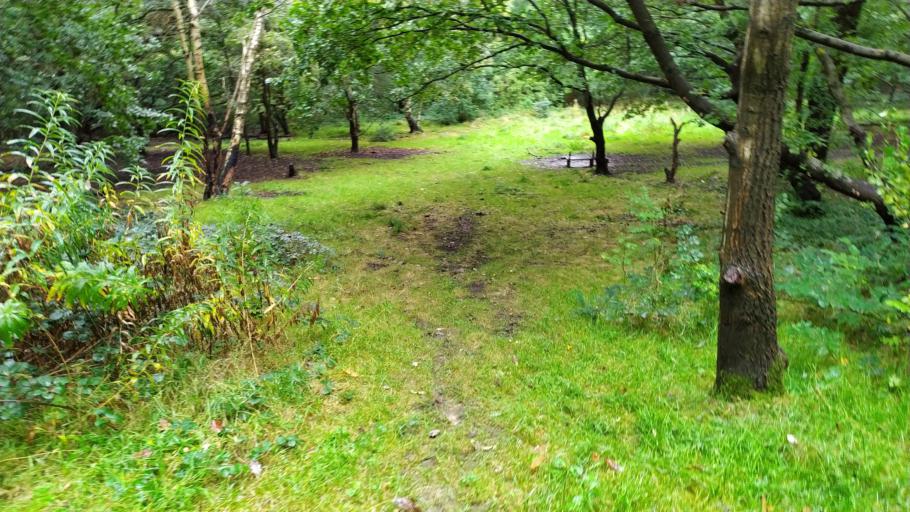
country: GB
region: England
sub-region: City and Borough of Leeds
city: Chapel Allerton
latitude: 53.8204
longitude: -1.5630
